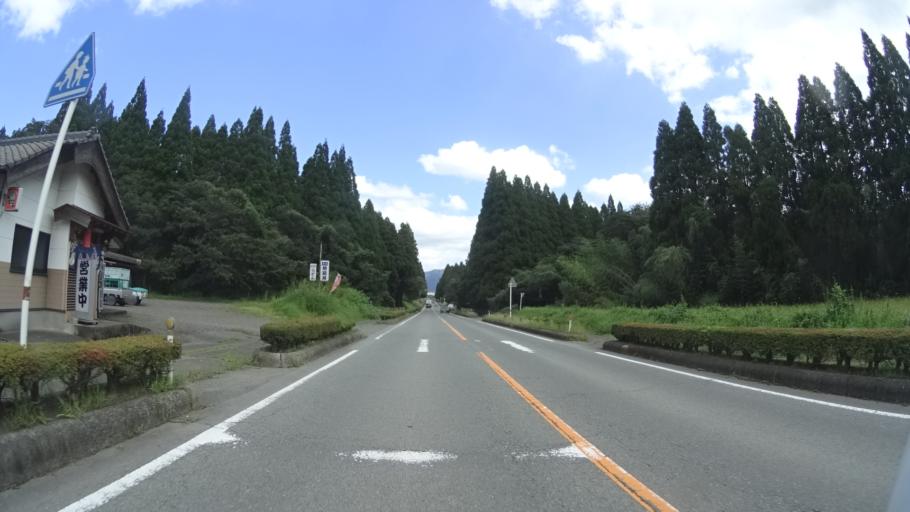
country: JP
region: Kumamoto
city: Aso
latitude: 32.8311
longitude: 131.0836
